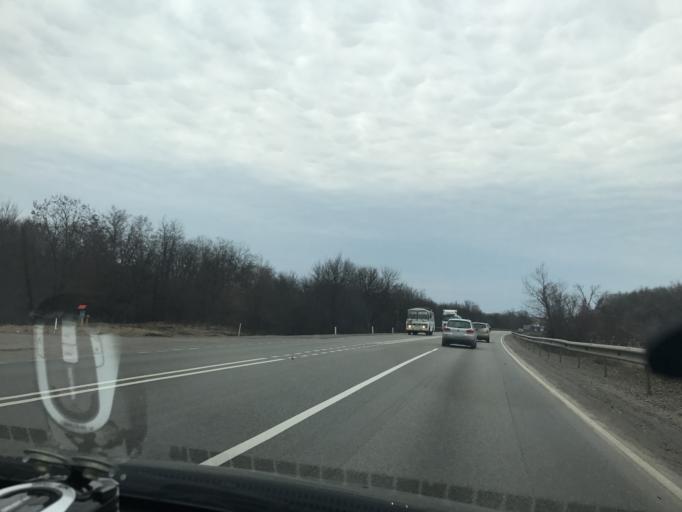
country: RU
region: Krasnodarskiy
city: Novoukrainskoye
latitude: 45.4042
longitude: 40.5466
